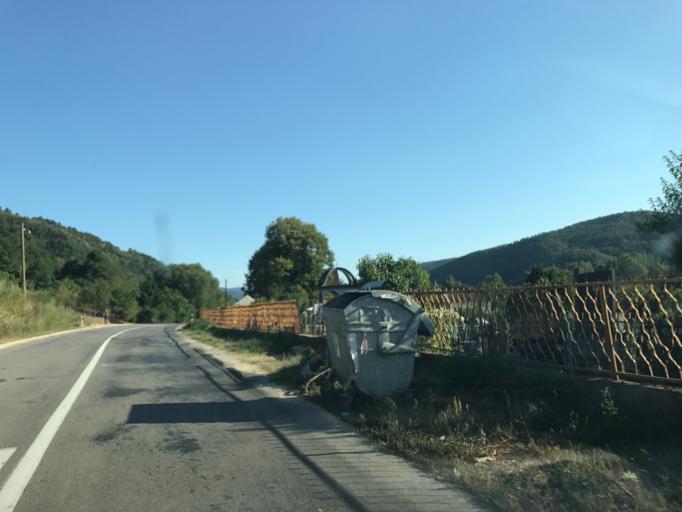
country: RO
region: Mehedinti
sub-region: Comuna Svinita
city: Svinita
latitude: 44.3969
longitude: 22.1745
